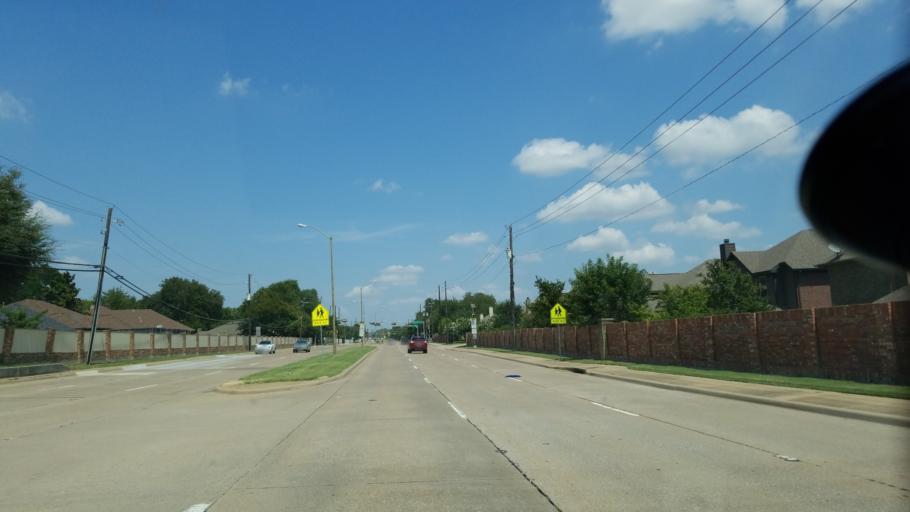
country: US
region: Texas
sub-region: Dallas County
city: Richardson
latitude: 32.9145
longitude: -96.7177
